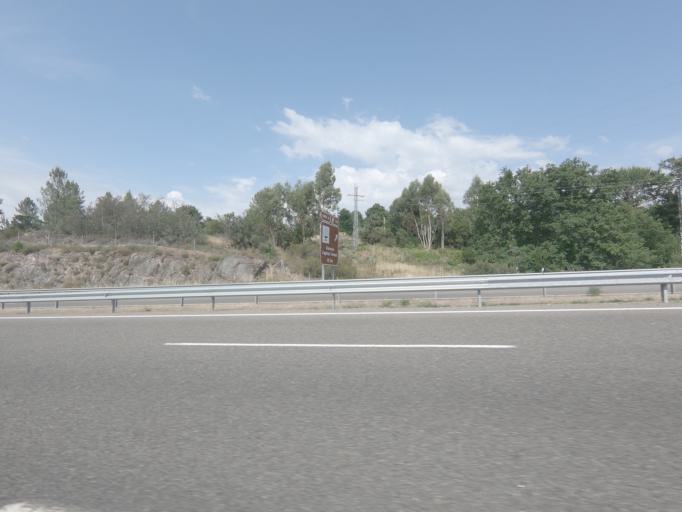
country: ES
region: Galicia
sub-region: Provincia de Ourense
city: Ourense
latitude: 42.2861
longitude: -7.8749
